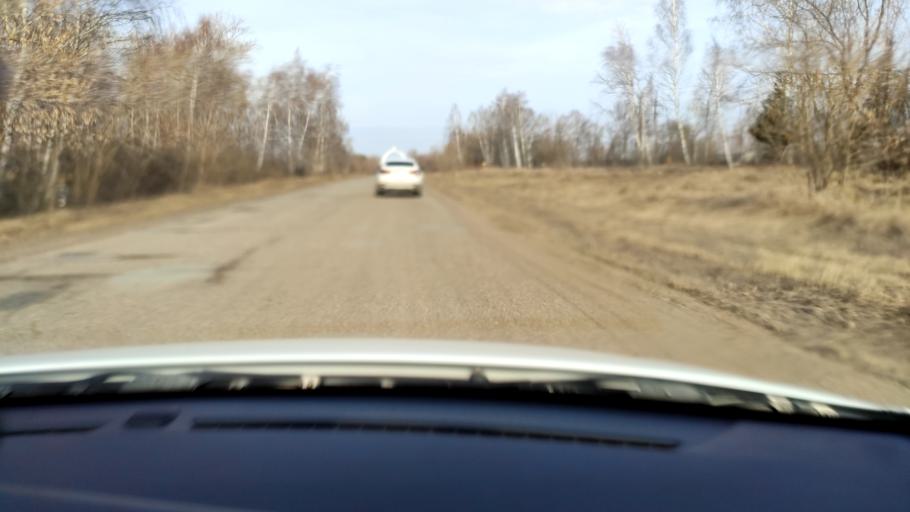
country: RU
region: Tatarstan
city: Stolbishchi
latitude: 55.7219
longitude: 49.2078
